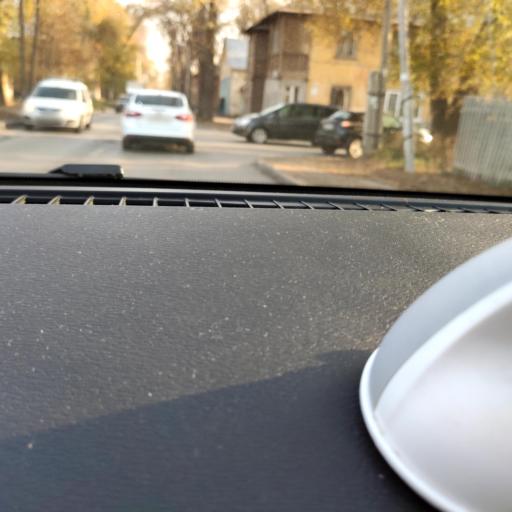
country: RU
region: Samara
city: Samara
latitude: 53.2400
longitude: 50.2581
